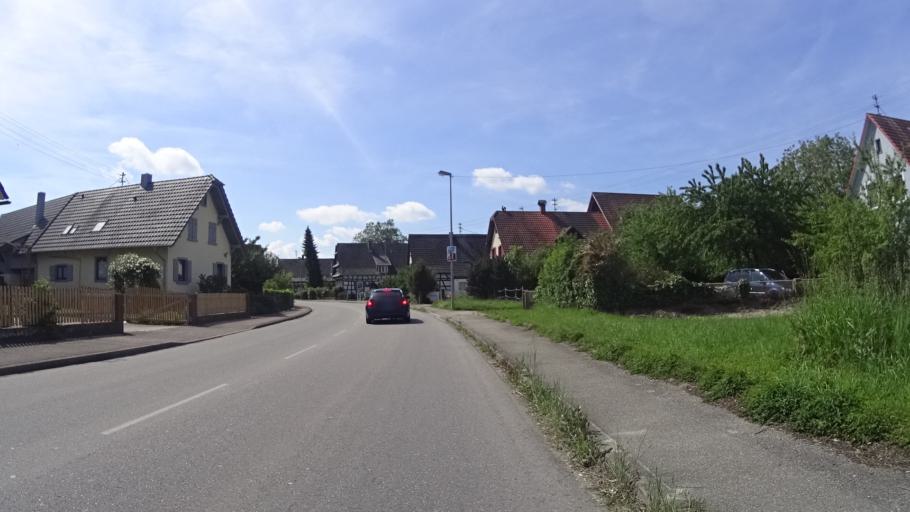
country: DE
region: Baden-Wuerttemberg
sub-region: Freiburg Region
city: Meissenheim
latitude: 48.4691
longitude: 7.8122
